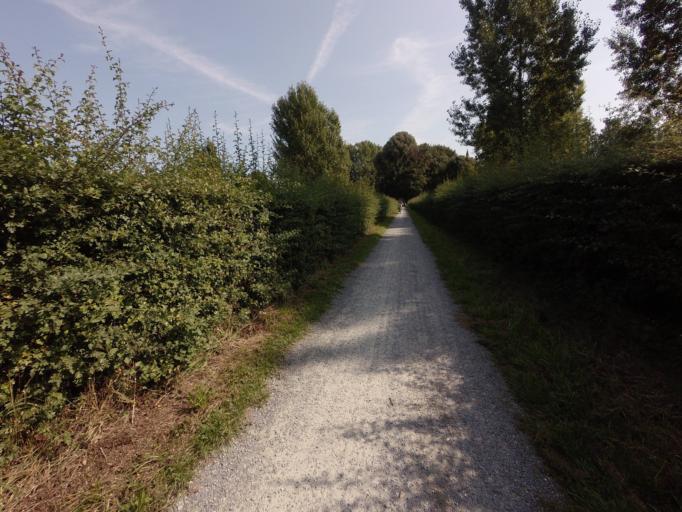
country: NL
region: Limburg
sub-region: Gemeente Roerdalen
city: Montfort
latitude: 51.1592
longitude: 5.9324
